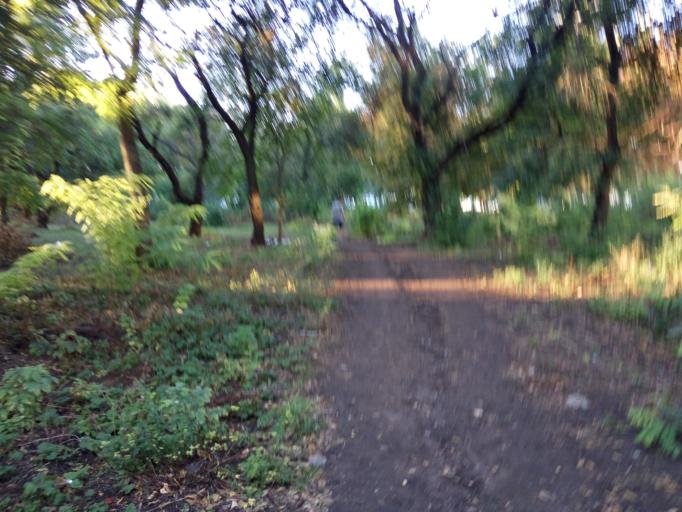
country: RU
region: Rostov
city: Rostov-na-Donu
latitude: 47.2427
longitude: 39.7585
